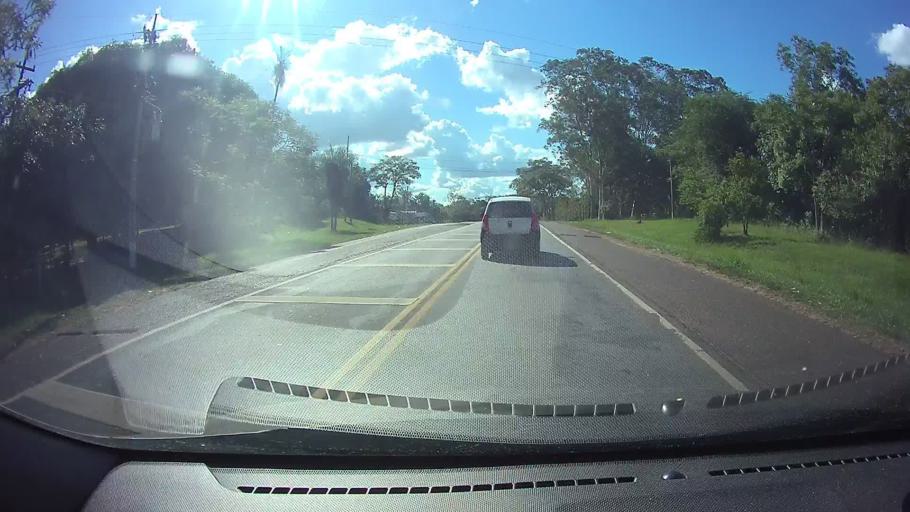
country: PY
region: Cordillera
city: Itacurubi de la Cordillera
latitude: -25.4638
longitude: -56.8799
